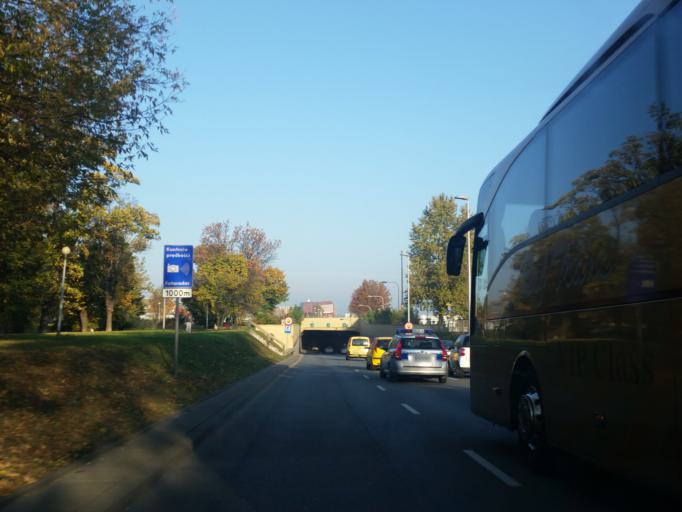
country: PL
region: Masovian Voivodeship
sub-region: Warszawa
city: Praga Polnoc
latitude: 52.2379
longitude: 21.0347
